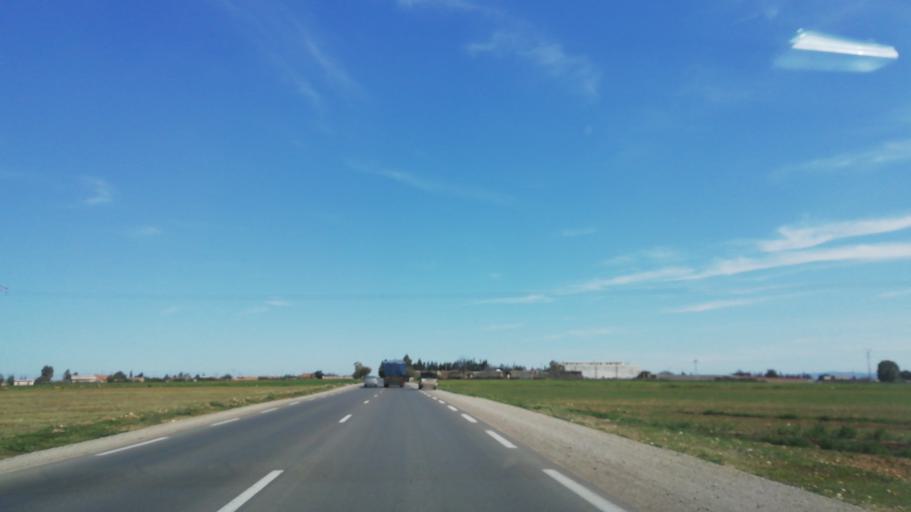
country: DZ
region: Mascara
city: Mascara
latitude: 35.4146
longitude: 0.3805
